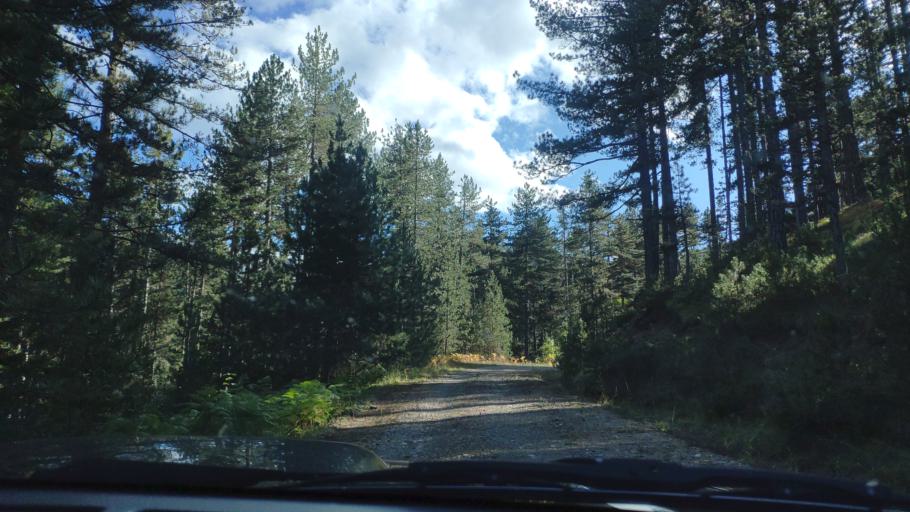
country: AL
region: Korce
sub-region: Rrethi i Devollit
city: Miras
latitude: 40.3935
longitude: 20.8868
